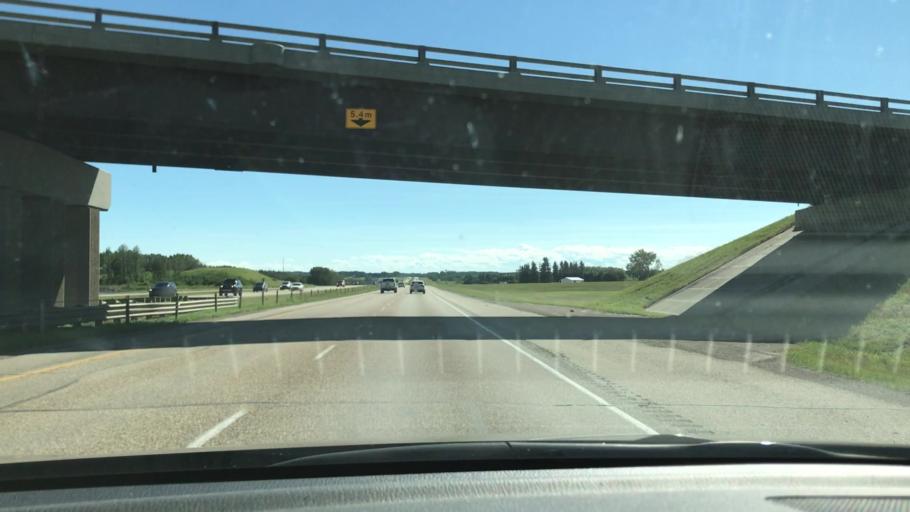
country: CA
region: Alberta
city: Penhold
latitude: 52.0028
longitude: -113.9620
